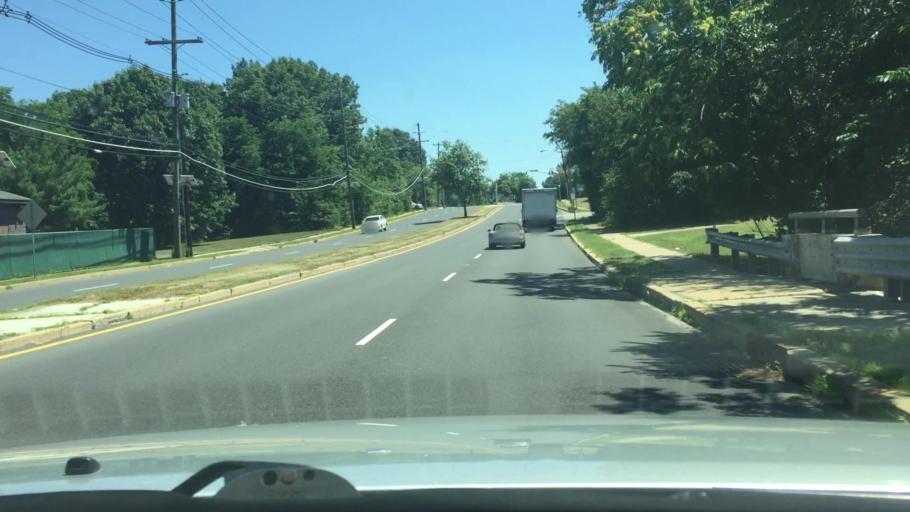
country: US
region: New Jersey
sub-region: Middlesex County
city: South River
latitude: 40.4345
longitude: -74.3929
